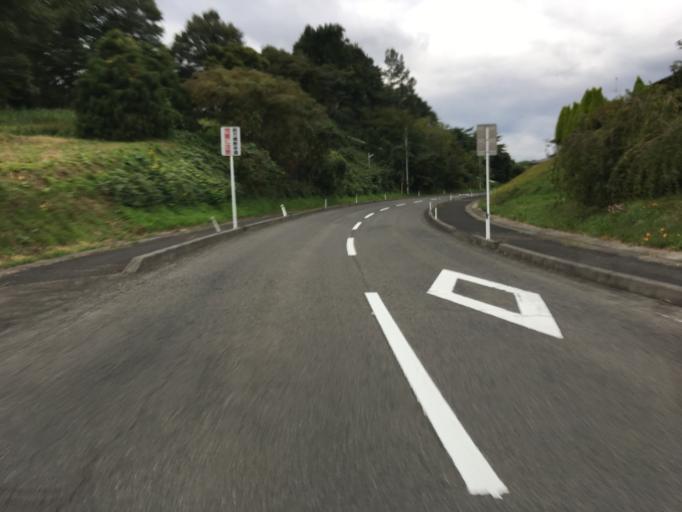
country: JP
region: Fukushima
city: Fukushima-shi
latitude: 37.6552
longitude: 140.5289
